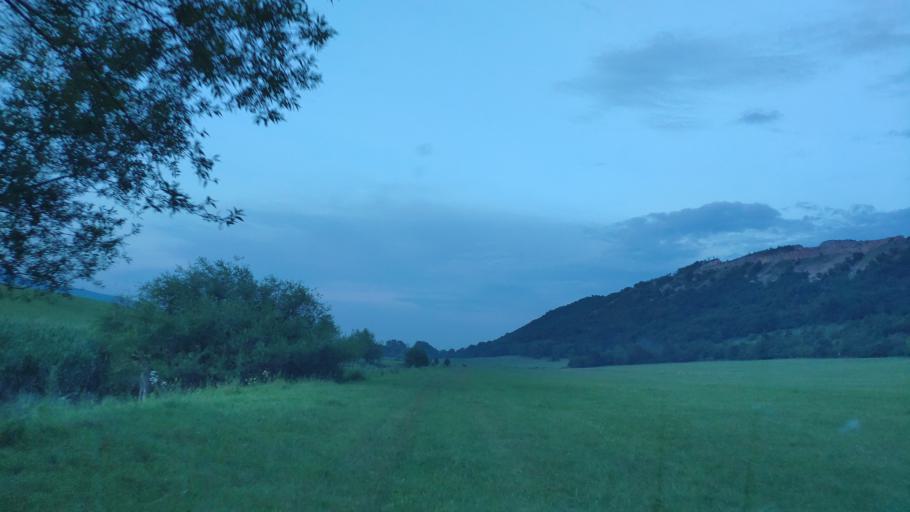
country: SK
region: Kosicky
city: Medzev
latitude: 48.5823
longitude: 20.7972
